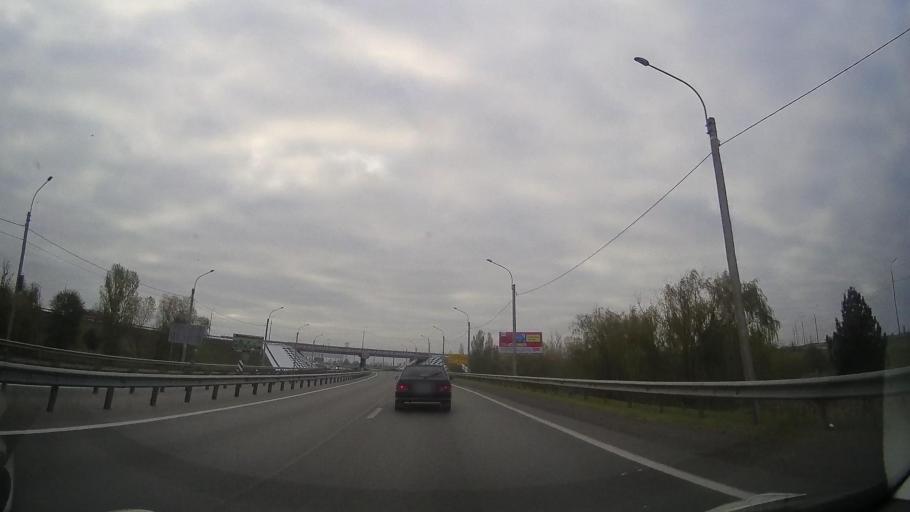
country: RU
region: Rostov
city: Bataysk
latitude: 47.1708
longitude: 39.7456
